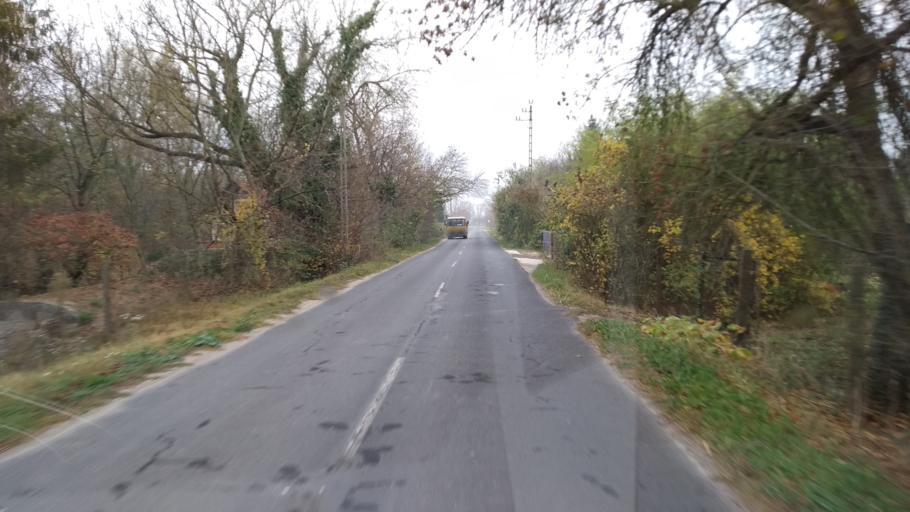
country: HU
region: Pest
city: Tahitotfalu
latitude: 47.7744
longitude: 19.0903
